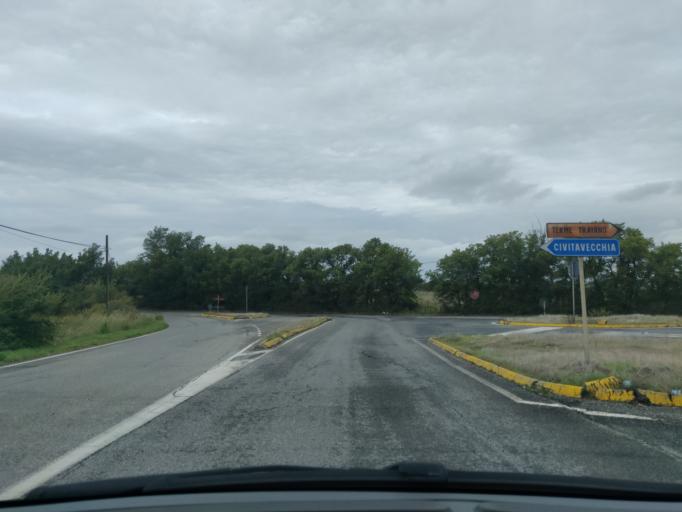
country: IT
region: Latium
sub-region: Citta metropolitana di Roma Capitale
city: Civitavecchia
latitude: 42.1079
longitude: 11.8335
